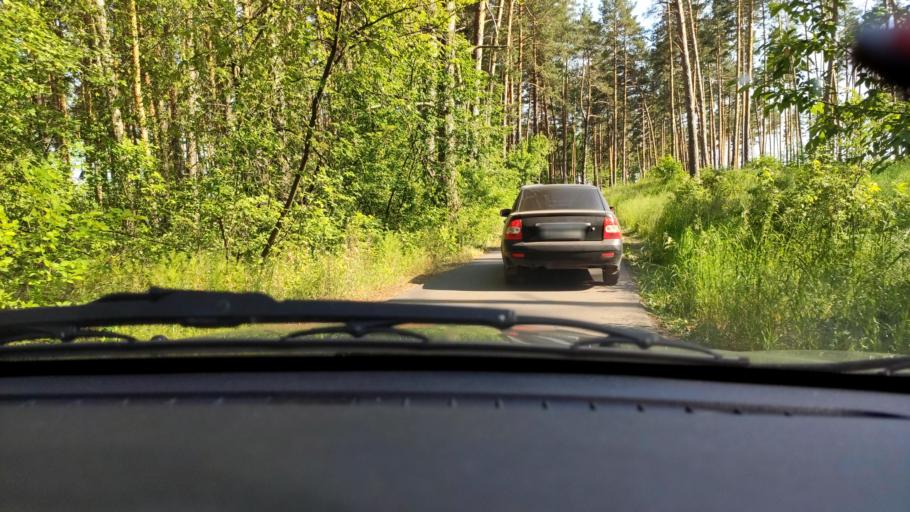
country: RU
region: Voronezj
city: Somovo
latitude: 51.7934
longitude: 39.3805
